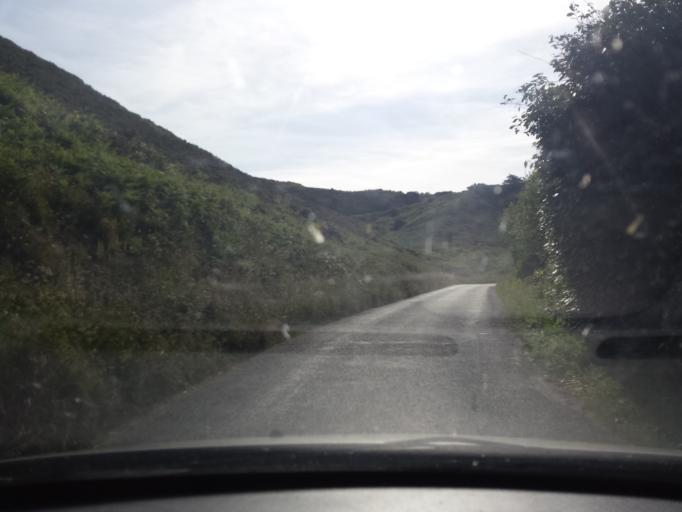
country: FR
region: Lower Normandy
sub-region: Departement de la Manche
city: Beaumont-Hague
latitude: 49.6904
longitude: -1.9338
